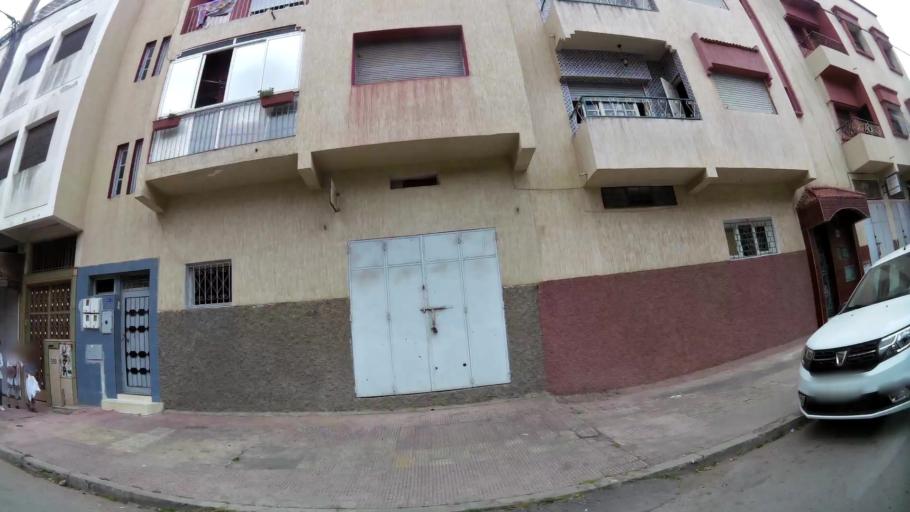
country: MA
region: Rabat-Sale-Zemmour-Zaer
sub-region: Rabat
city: Rabat
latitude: 33.9799
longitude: -6.8174
